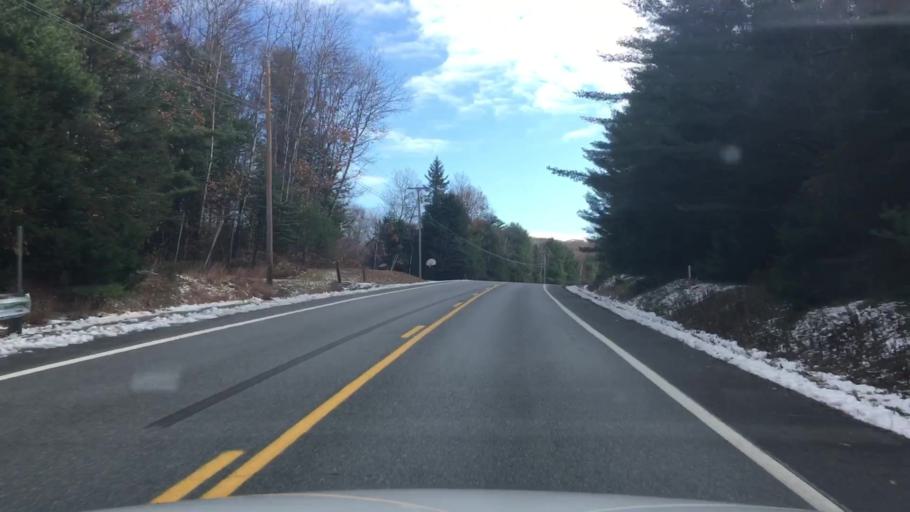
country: US
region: Maine
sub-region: Kennebec County
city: Winthrop
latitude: 44.3328
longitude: -70.0076
